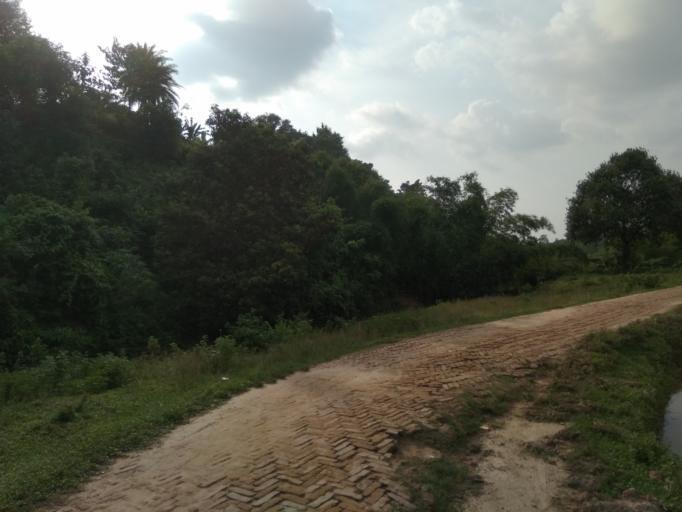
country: BD
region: Chittagong
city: Manikchari
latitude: 22.9336
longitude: 91.9102
